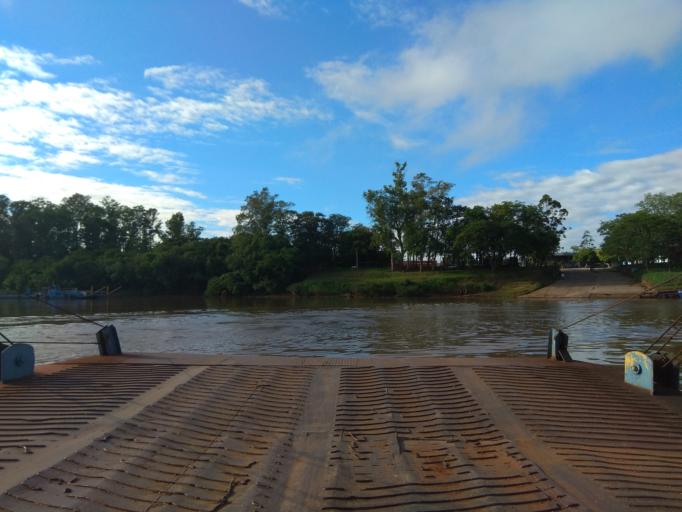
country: AR
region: Misiones
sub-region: Departamento de San Javier
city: San Javier
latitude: -27.8968
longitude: -55.1381
